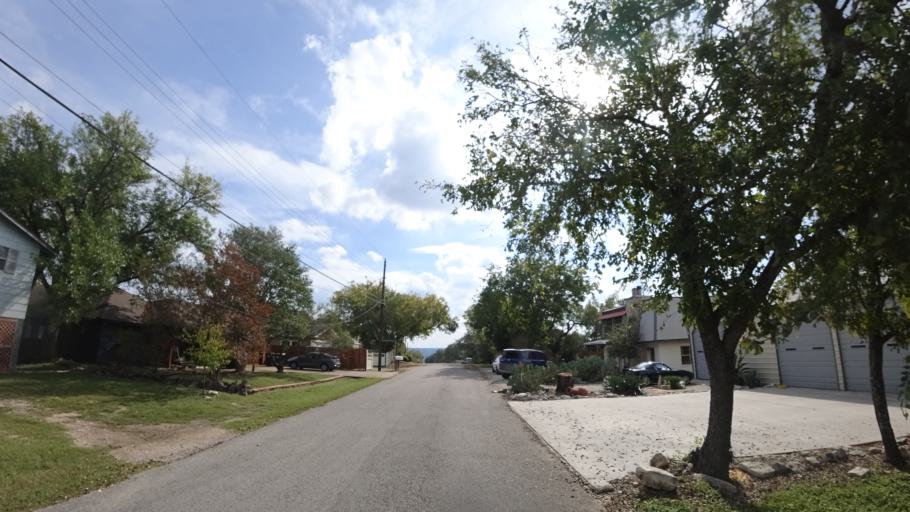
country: US
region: Texas
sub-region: Travis County
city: Hudson Bend
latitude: 30.3834
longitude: -97.9169
